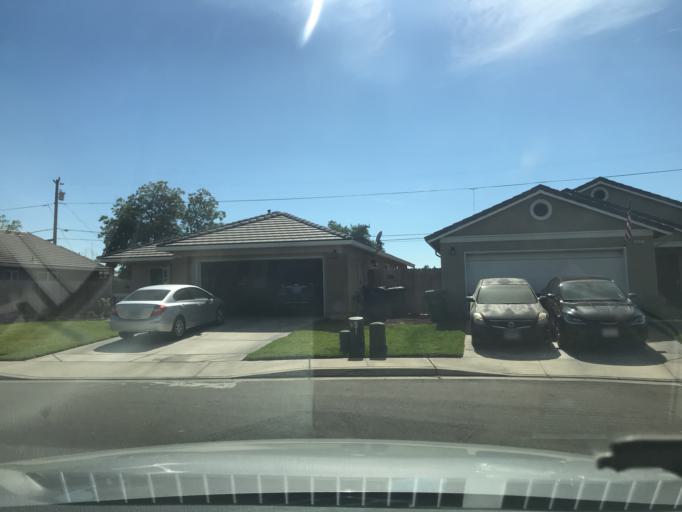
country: US
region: California
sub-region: Merced County
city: Merced
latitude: 37.3307
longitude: -120.5268
